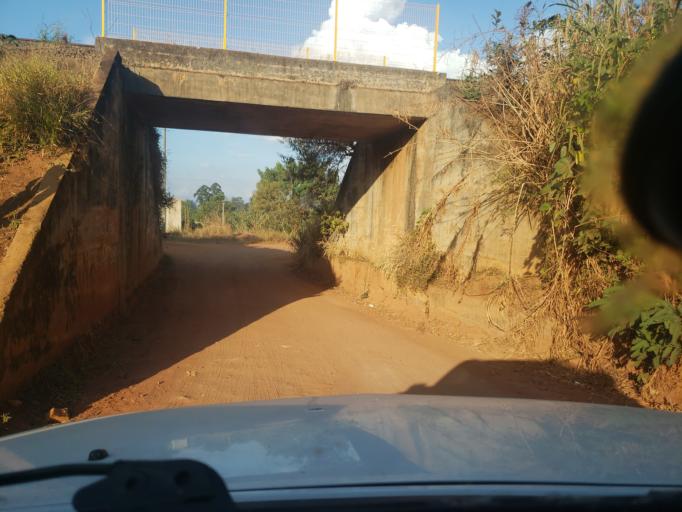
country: BR
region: Sao Paulo
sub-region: Mogi-Mirim
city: Mogi Mirim
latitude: -22.4572
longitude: -46.9412
